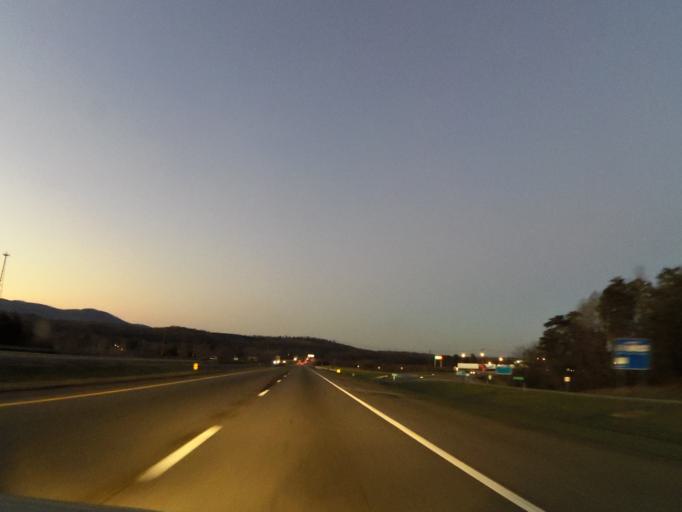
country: US
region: Tennessee
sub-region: Cocke County
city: Newport
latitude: 35.8777
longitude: -83.1861
